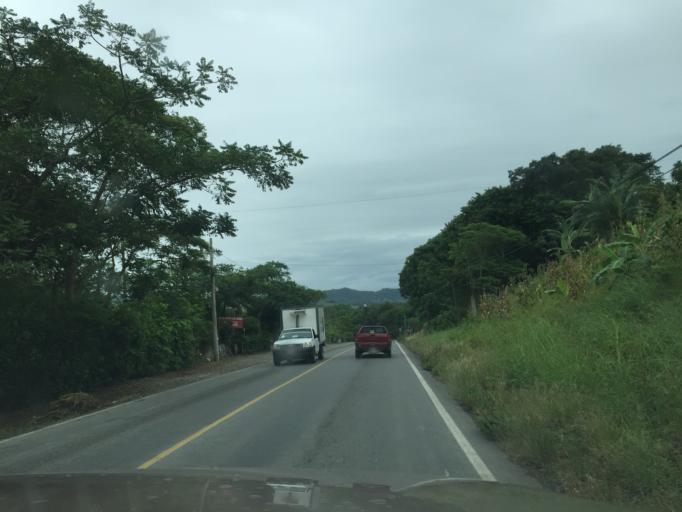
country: MX
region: Veracruz
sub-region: Papantla
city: El Chote
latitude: 20.4382
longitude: -97.3879
